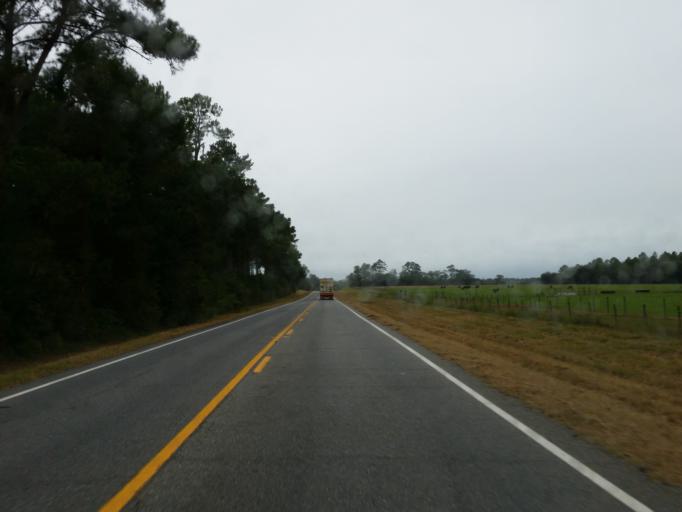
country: US
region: Georgia
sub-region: Berrien County
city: Nashville
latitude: 31.1174
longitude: -83.3117
